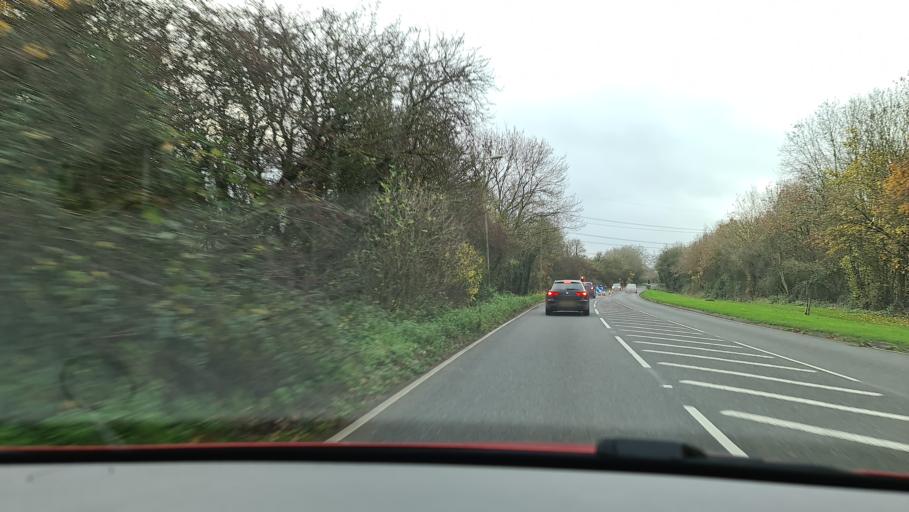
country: GB
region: England
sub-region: Oxfordshire
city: Bicester
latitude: 51.8506
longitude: -1.0900
